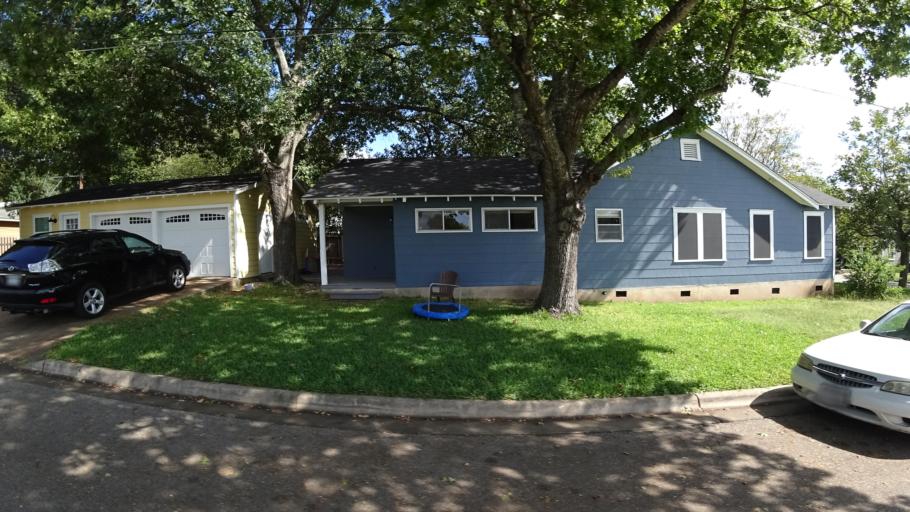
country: US
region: Texas
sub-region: Travis County
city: Austin
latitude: 30.3070
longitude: -97.7215
